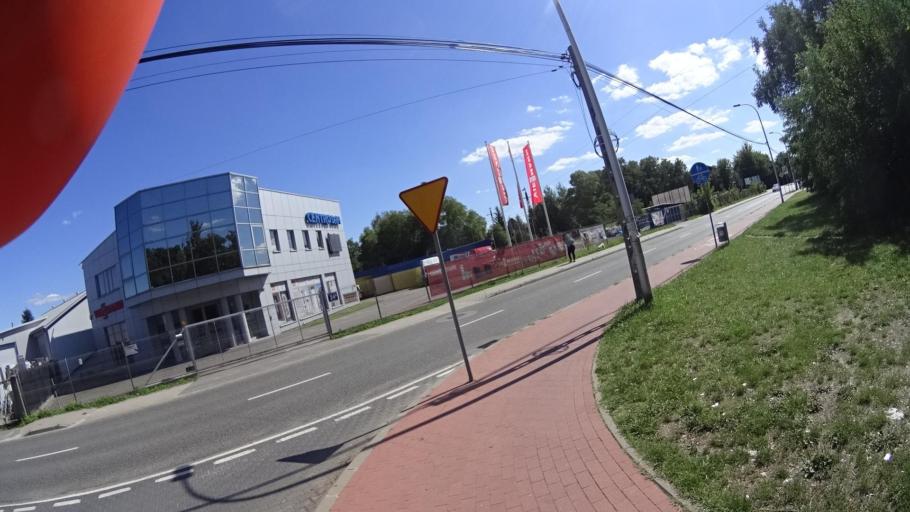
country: PL
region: Masovian Voivodeship
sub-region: Powiat piaseczynski
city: Piaseczno
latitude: 52.0804
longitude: 21.0398
